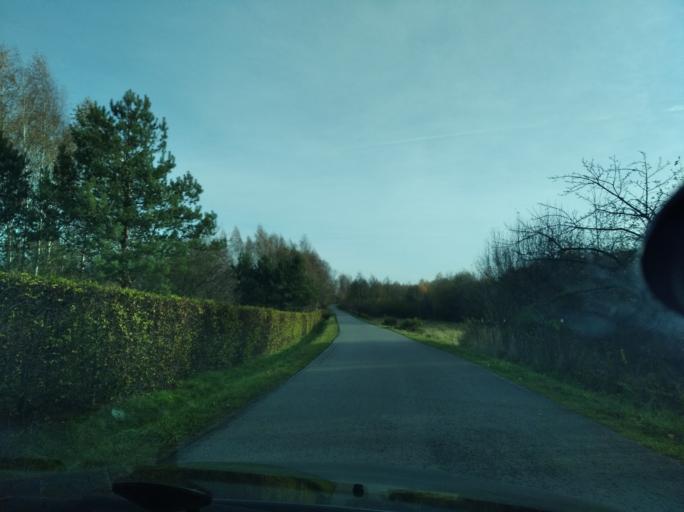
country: PL
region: Subcarpathian Voivodeship
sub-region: Powiat rzeszowski
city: Siedliska
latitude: 49.9347
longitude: 21.9646
